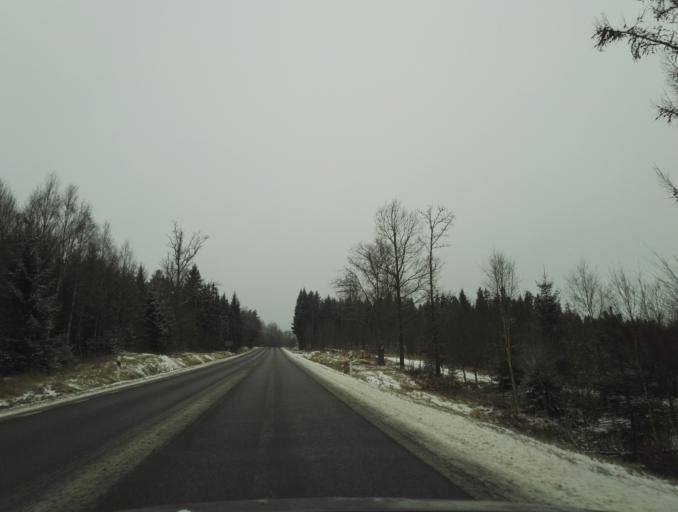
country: SE
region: Kronoberg
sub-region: Vaxjo Kommun
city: Gemla
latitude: 56.8209
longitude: 14.6884
